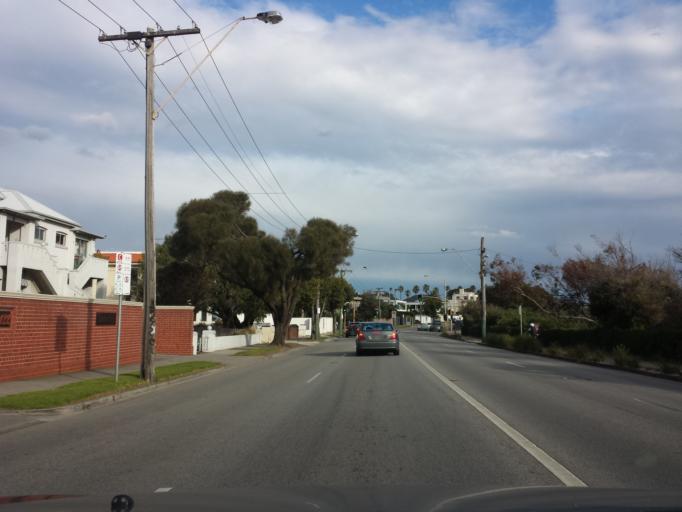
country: AU
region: Victoria
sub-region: Bayside
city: North Brighton
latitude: -37.9180
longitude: 144.9877
